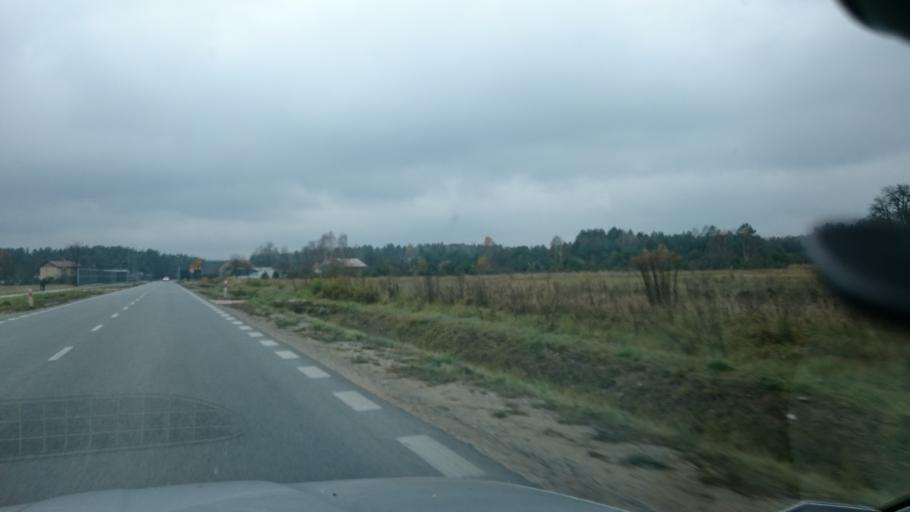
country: PL
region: Swietokrzyskie
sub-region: Powiat konecki
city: Konskie
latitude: 51.1315
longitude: 20.3612
